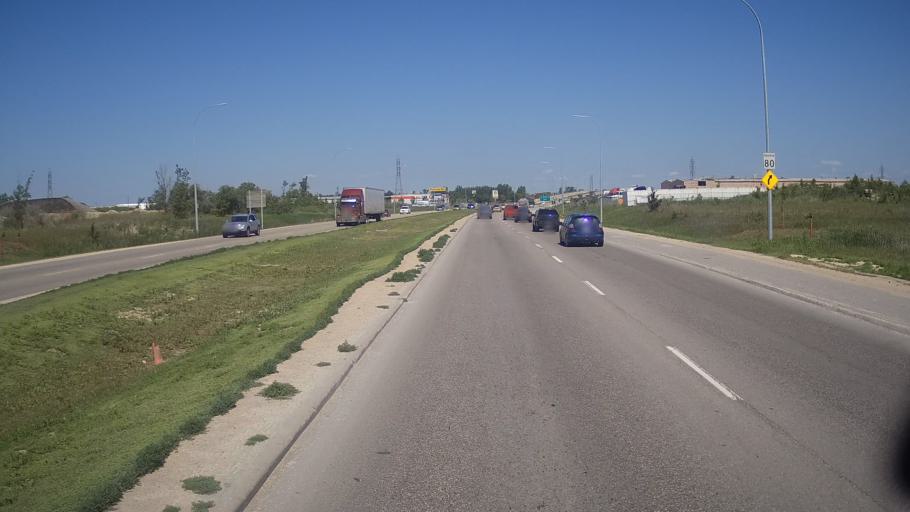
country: CA
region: Manitoba
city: Winnipeg
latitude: 49.8873
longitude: -97.0722
